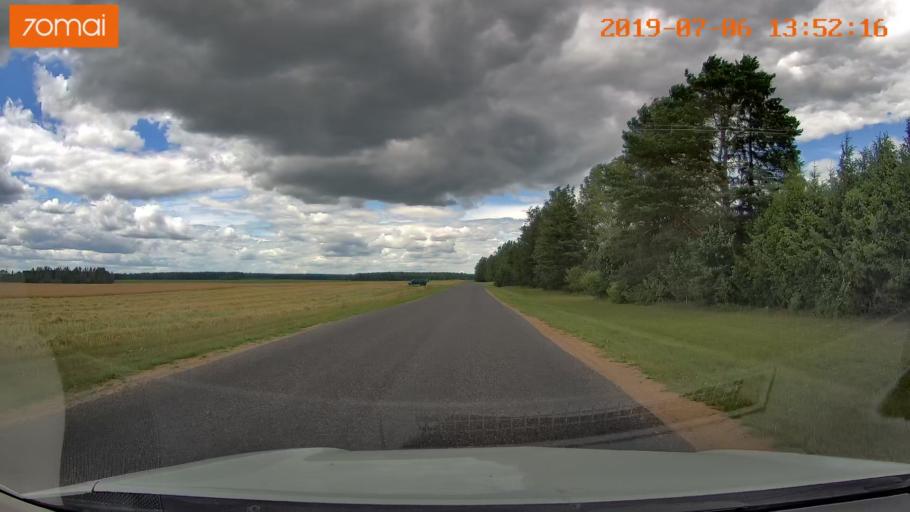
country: BY
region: Minsk
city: Ivyanyets
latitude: 53.7186
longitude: 26.8299
